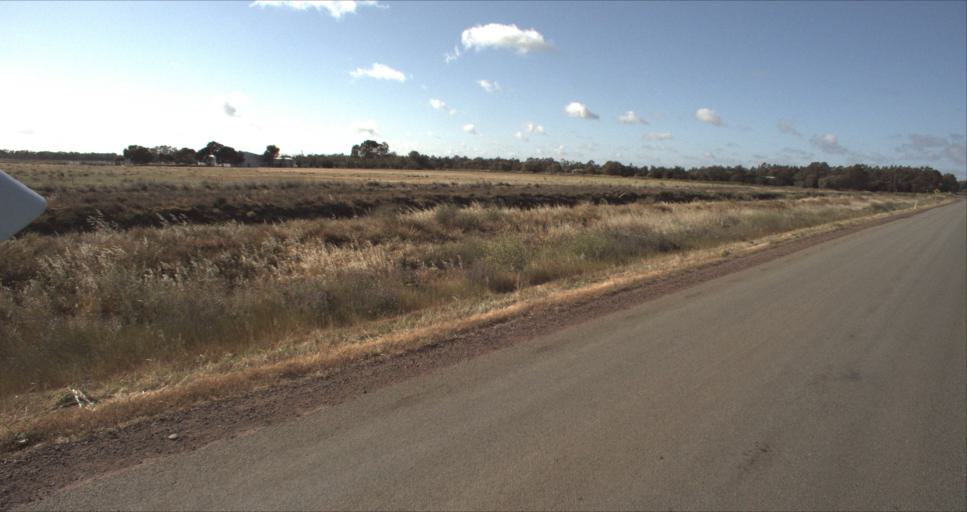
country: AU
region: New South Wales
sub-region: Leeton
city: Leeton
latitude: -34.5241
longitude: 146.3900
